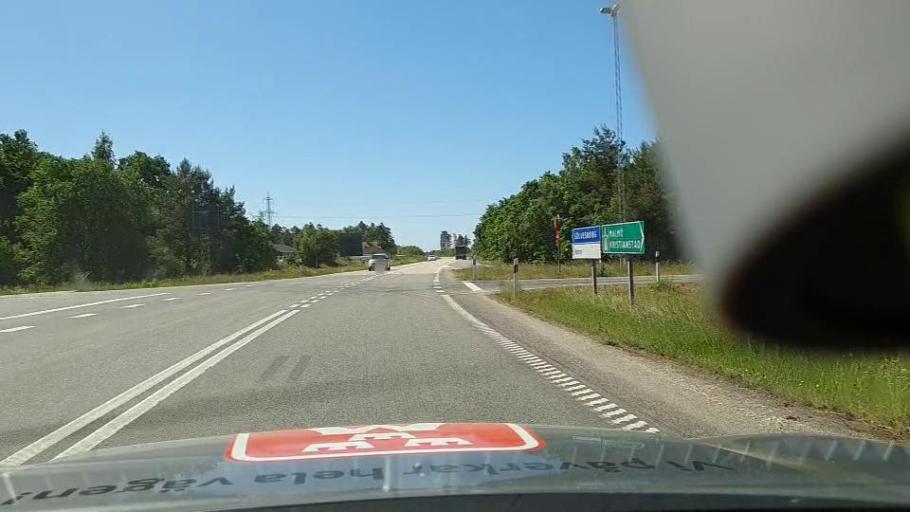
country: SE
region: Blekinge
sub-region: Solvesborgs Kommun
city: Soelvesborg
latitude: 56.0646
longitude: 14.5662
